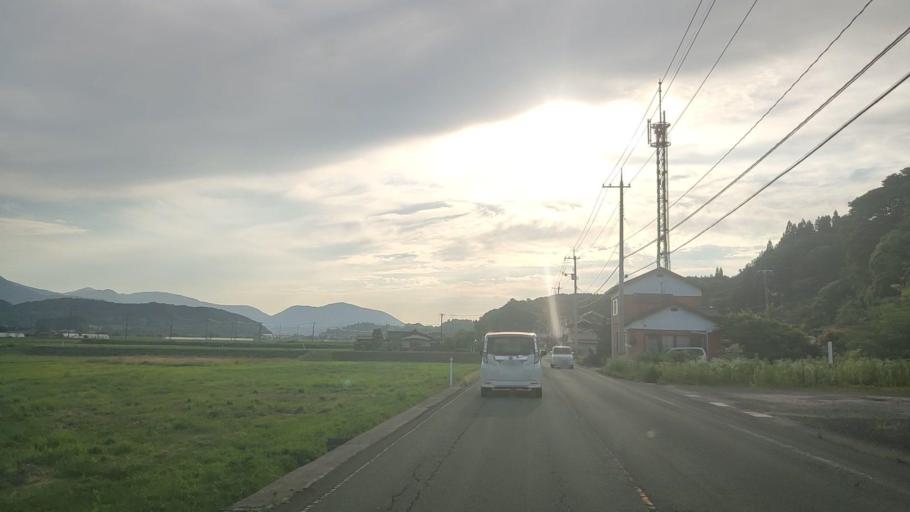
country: JP
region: Tottori
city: Kurayoshi
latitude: 35.2800
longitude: 133.6718
